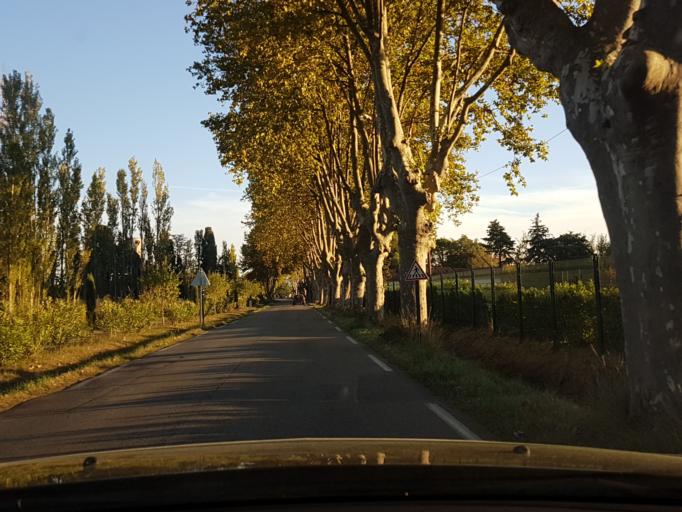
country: FR
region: Provence-Alpes-Cote d'Azur
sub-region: Departement des Bouches-du-Rhone
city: Saint-Andiol
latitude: 43.8295
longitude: 4.9444
